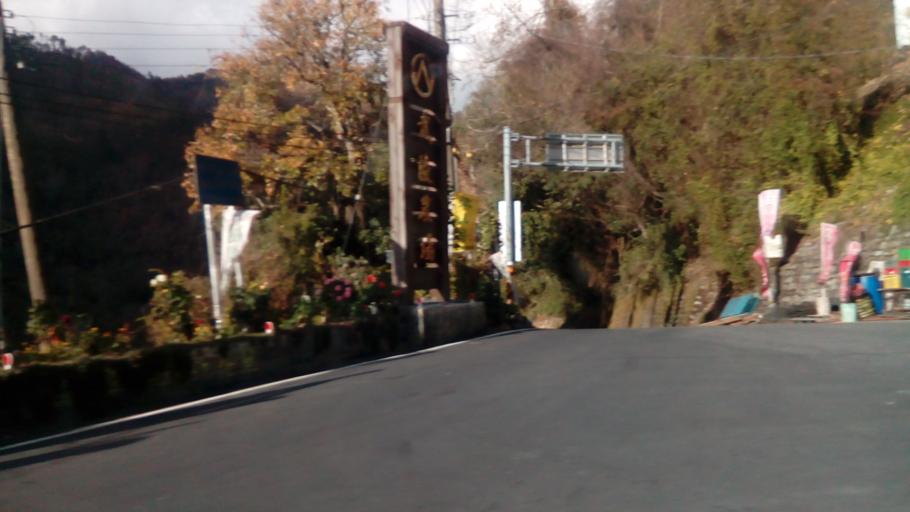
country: TW
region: Taiwan
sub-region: Hualien
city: Hualian
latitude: 24.3497
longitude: 121.3222
